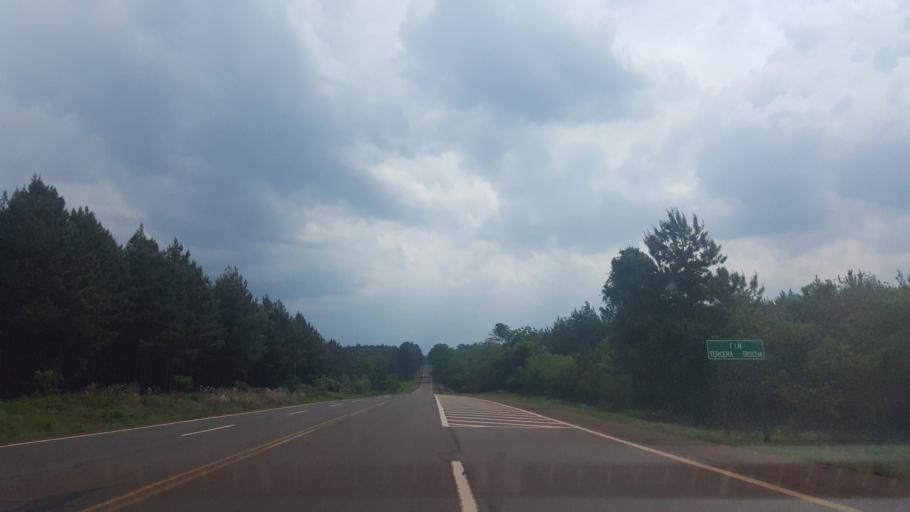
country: AR
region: Misiones
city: Santo Pipo
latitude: -27.1068
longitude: -55.3291
